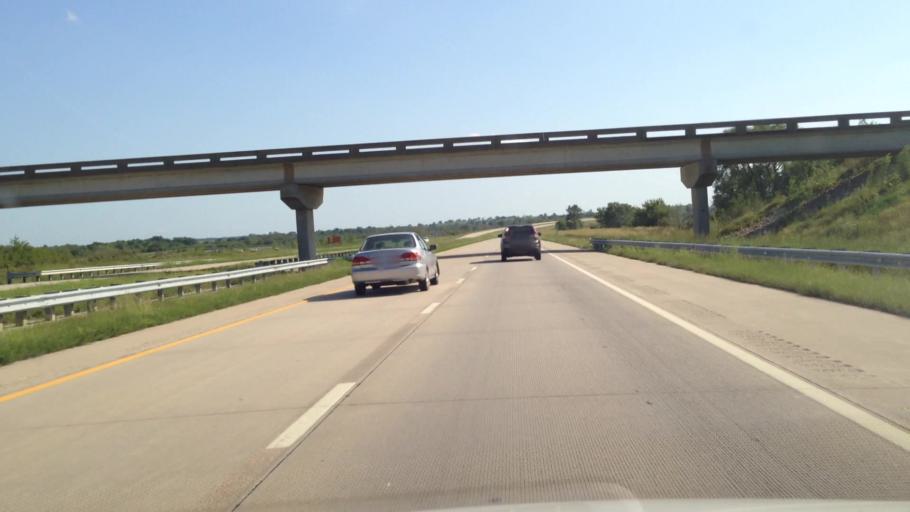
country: US
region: Kansas
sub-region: Bourbon County
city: Fort Scott
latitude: 37.9786
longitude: -94.7050
